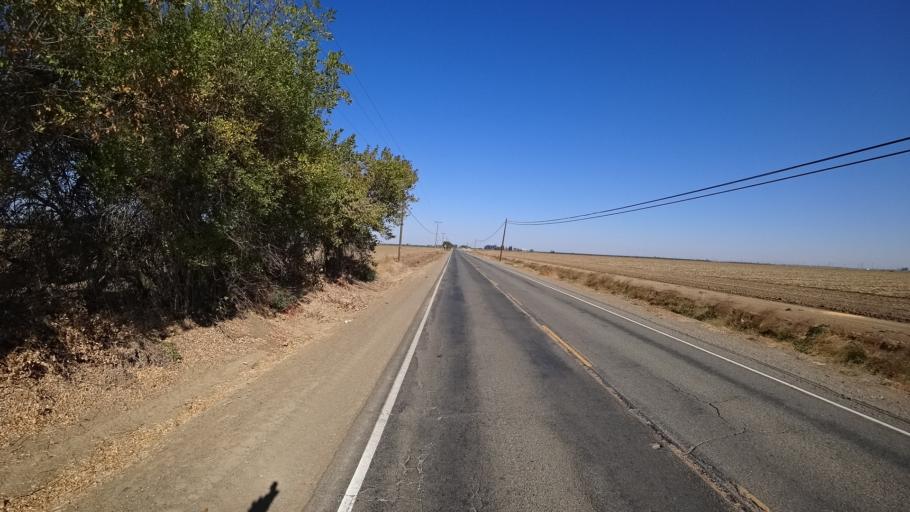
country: US
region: California
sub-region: Yolo County
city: Cottonwood
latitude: 38.6358
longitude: -121.9714
